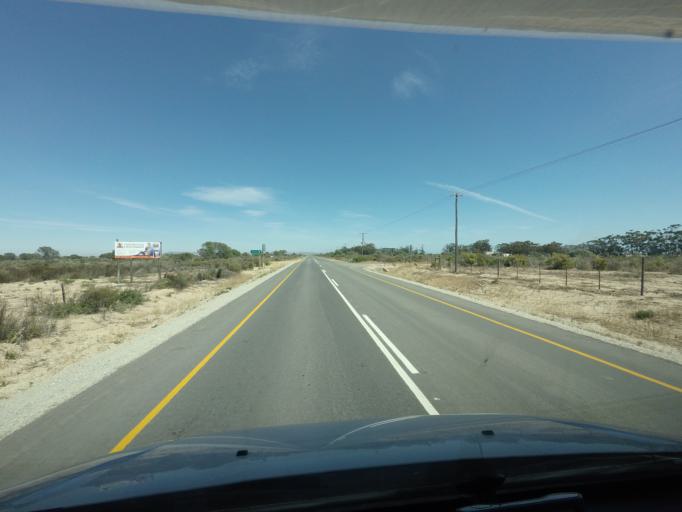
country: ZA
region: Western Cape
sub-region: West Coast District Municipality
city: Vredenburg
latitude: -32.7950
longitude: 18.2468
